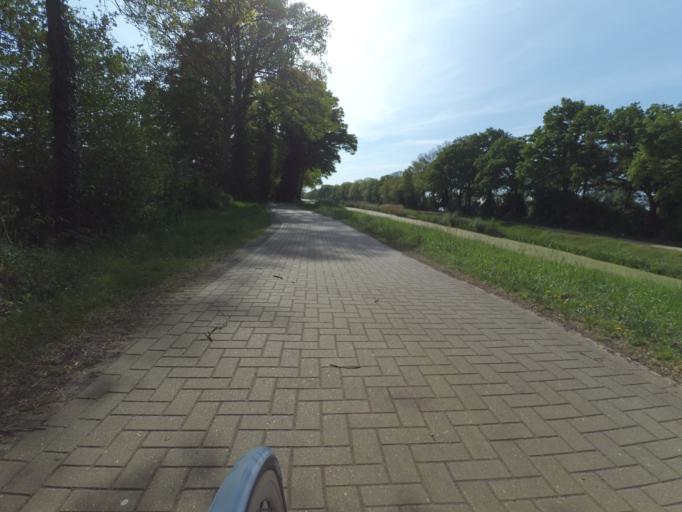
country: NL
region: Overijssel
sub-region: Gemeente Tubbergen
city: Tubbergen
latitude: 52.3728
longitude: 6.8544
